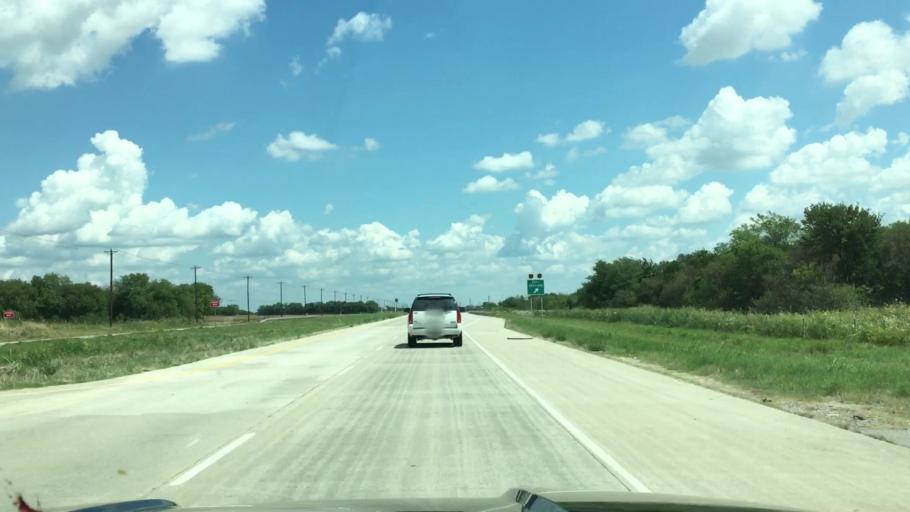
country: US
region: Texas
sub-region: Tarrant County
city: Haslet
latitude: 33.0354
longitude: -97.3625
